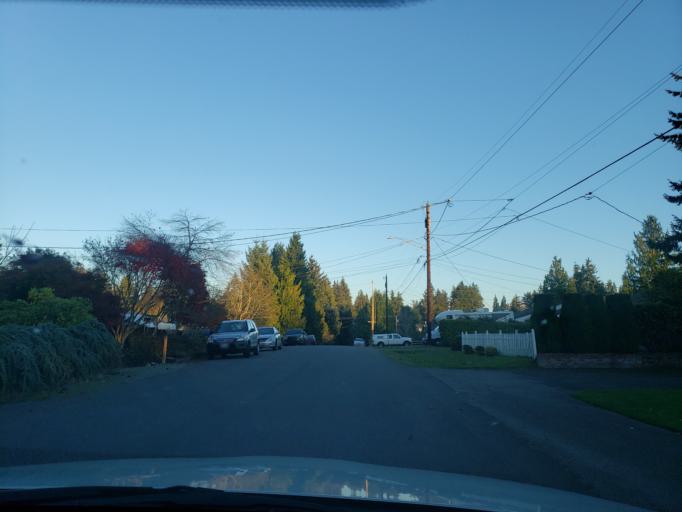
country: US
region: Washington
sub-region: Snohomish County
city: Edmonds
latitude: 47.8044
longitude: -122.3631
